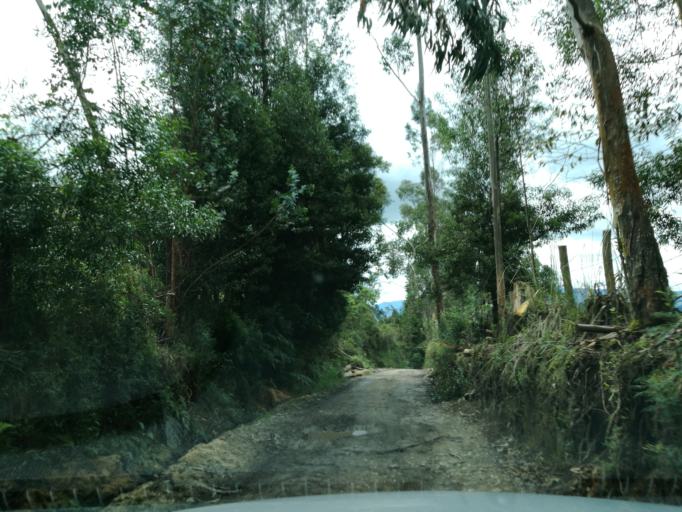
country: CO
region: Boyaca
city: Arcabuco
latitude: 5.7522
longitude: -73.4571
